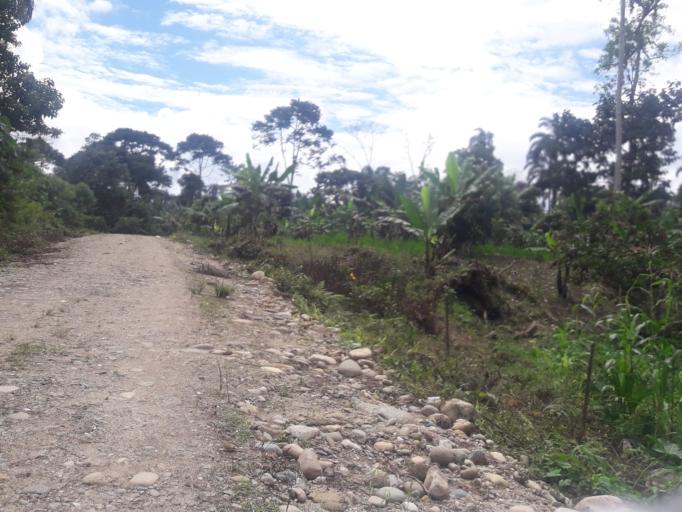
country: EC
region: Napo
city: Tena
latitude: -0.9758
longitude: -77.8511
